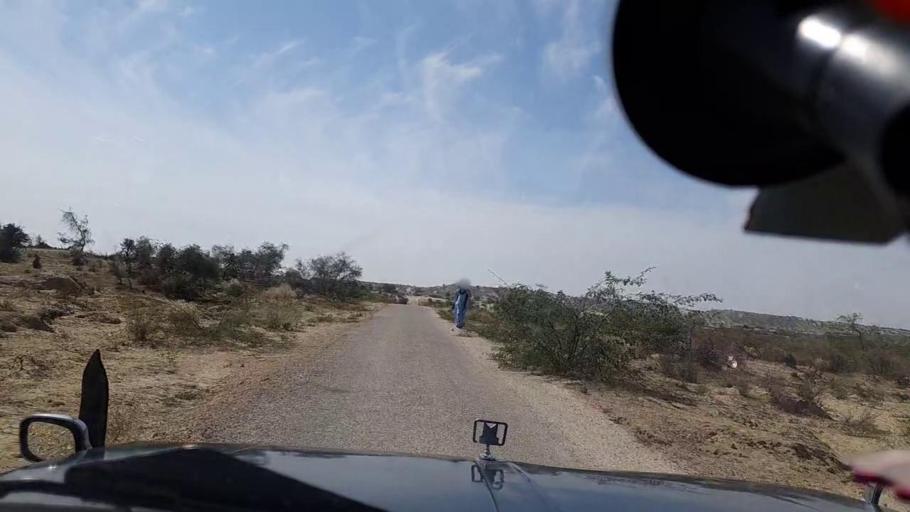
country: PK
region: Sindh
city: Diplo
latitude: 24.3754
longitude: 69.5841
